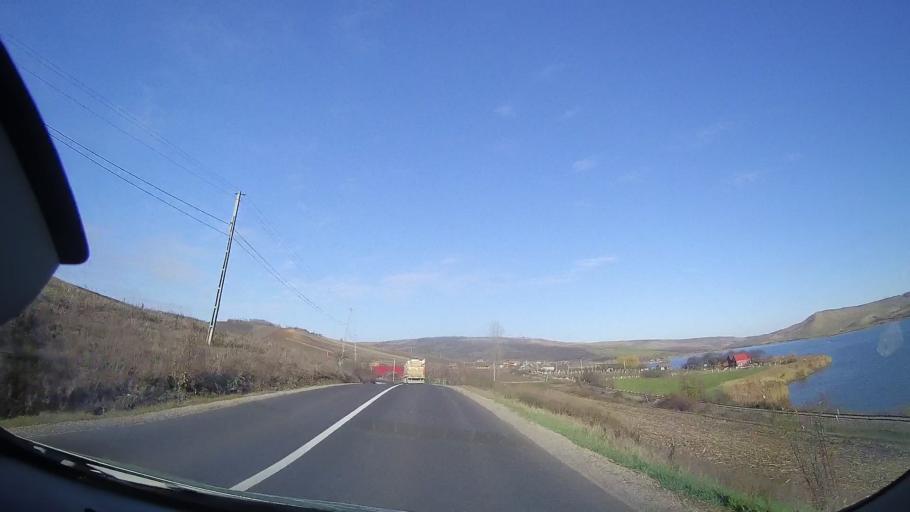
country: RO
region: Mures
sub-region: Comuna Zau De Campie
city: Zau de Campie
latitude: 46.6273
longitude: 24.1330
